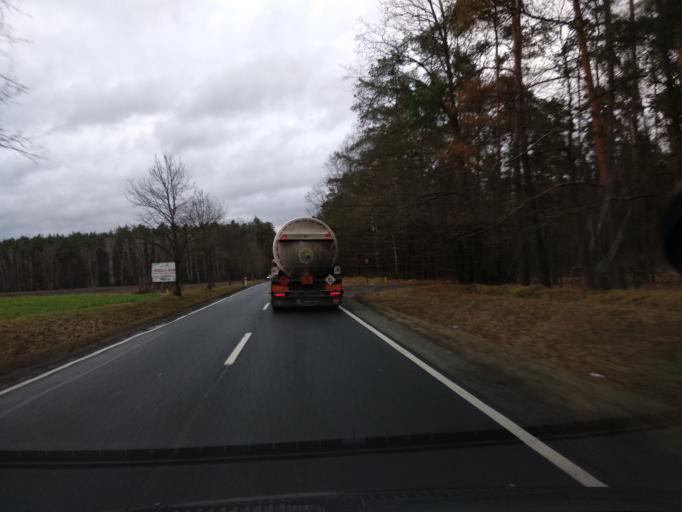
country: PL
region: Lower Silesian Voivodeship
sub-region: Powiat olesnicki
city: Twardogora
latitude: 51.2823
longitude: 17.5040
